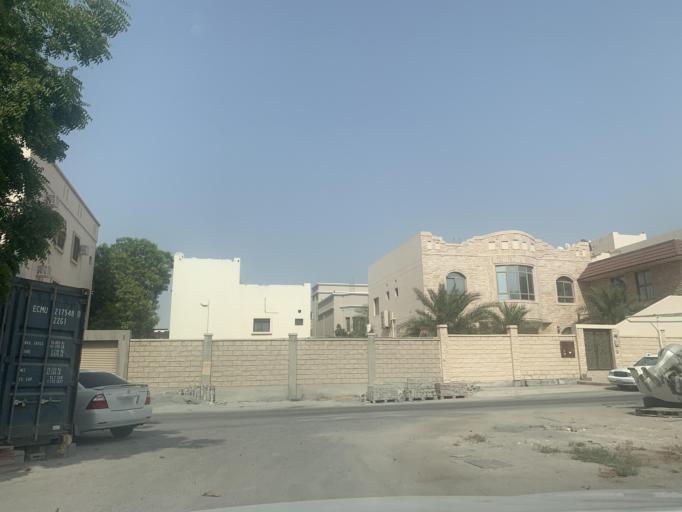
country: BH
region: Manama
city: Jidd Hafs
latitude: 26.2203
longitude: 50.4717
